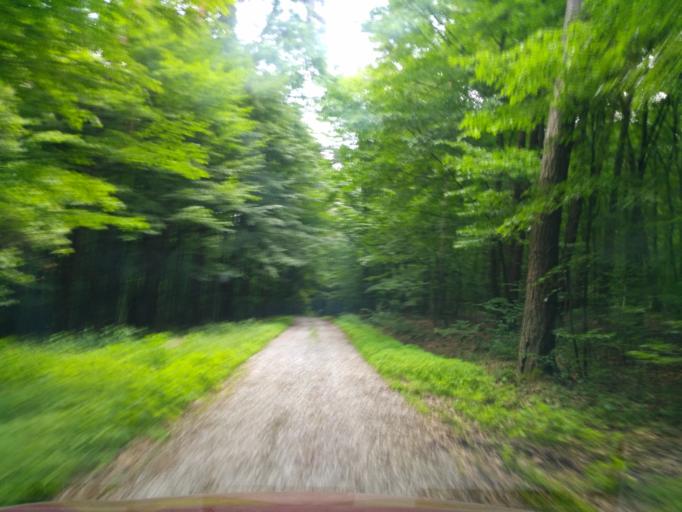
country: SK
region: Kosicky
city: Moldava nad Bodvou
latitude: 48.6537
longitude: 21.0491
